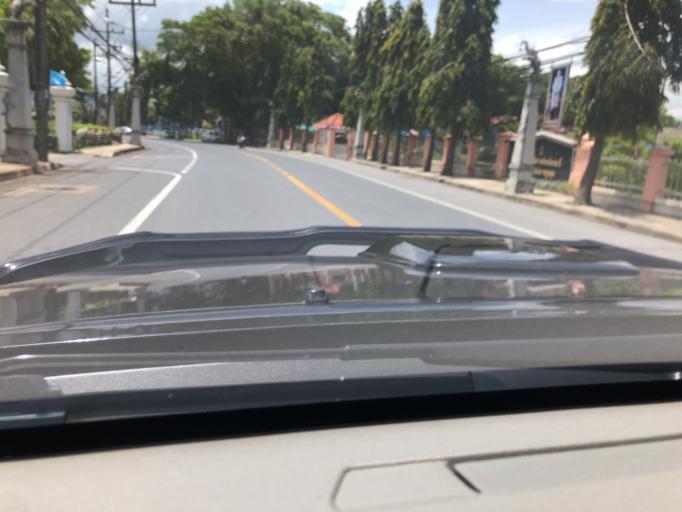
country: TH
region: Krabi
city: Krabi
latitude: 8.0588
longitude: 98.9185
